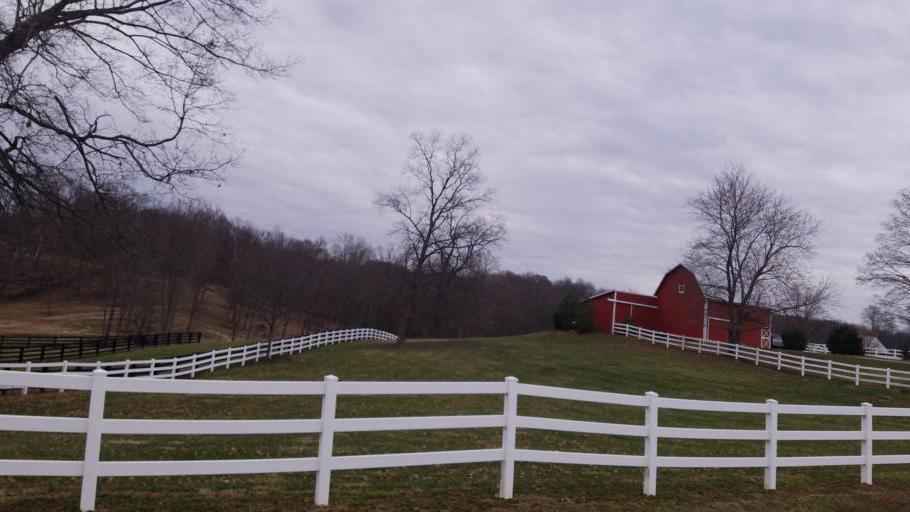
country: US
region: Ohio
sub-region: Knox County
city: Fredericktown
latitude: 40.5022
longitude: -82.4950
